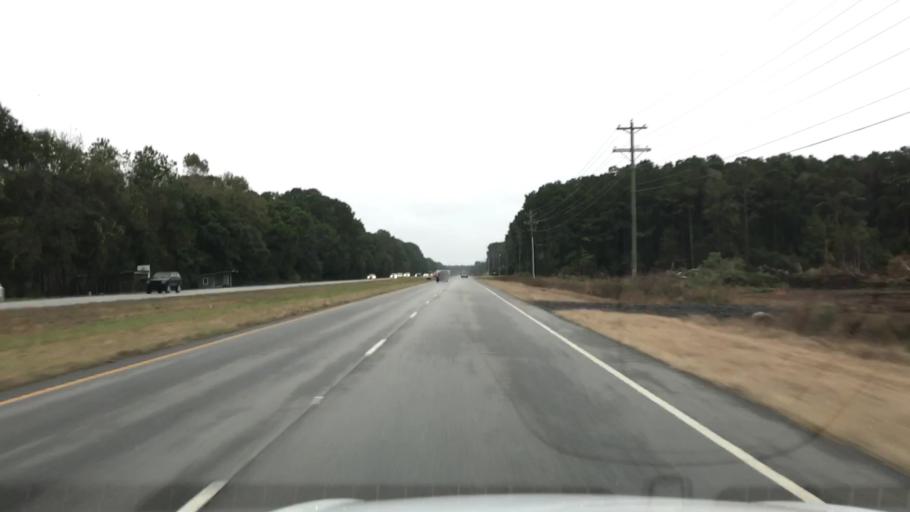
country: US
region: South Carolina
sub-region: Charleston County
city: Isle of Palms
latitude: 32.9068
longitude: -79.7258
